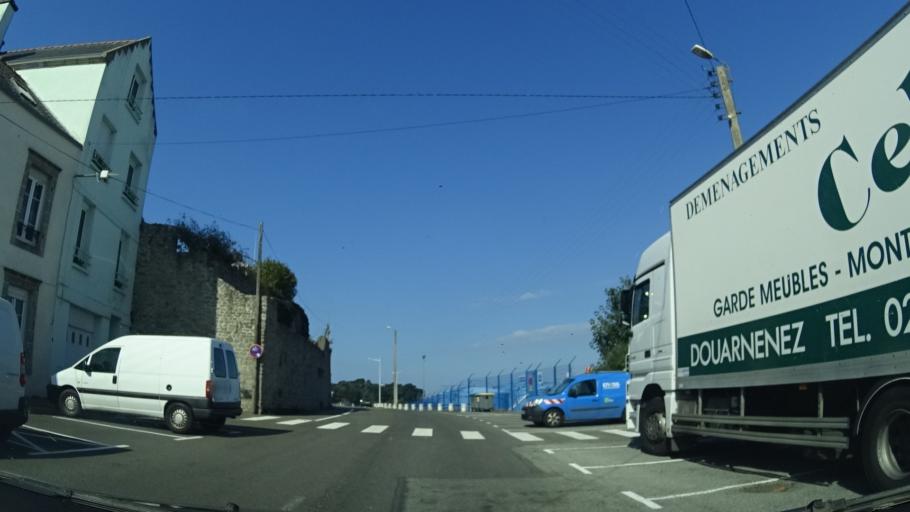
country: FR
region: Brittany
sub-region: Departement du Finistere
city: Douarnenez
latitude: 48.0966
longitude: -4.3279
